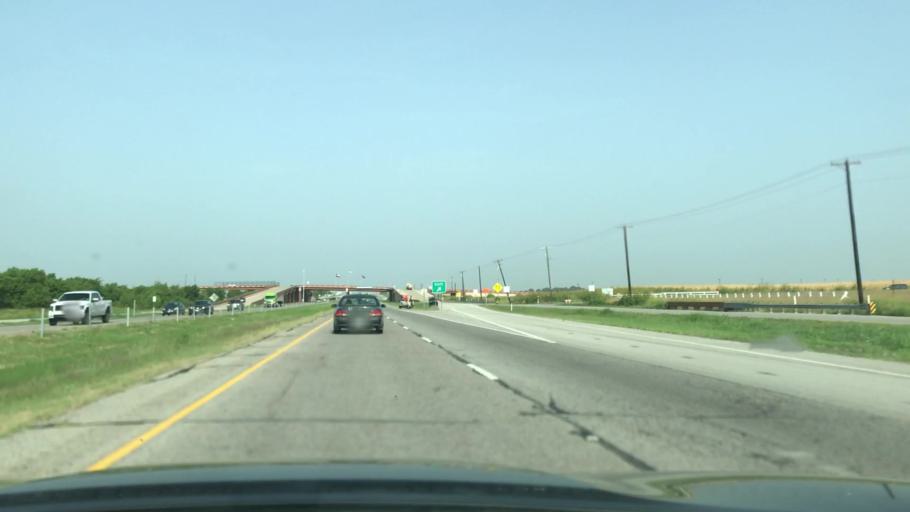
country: US
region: Texas
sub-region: Kaufman County
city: Talty
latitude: 32.7404
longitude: -96.4075
